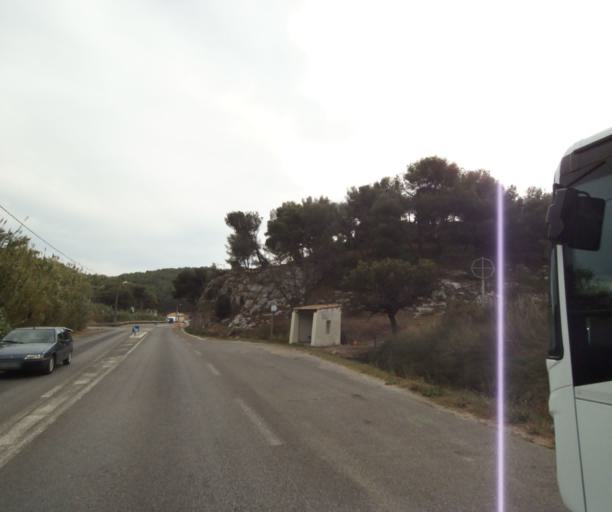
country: FR
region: Provence-Alpes-Cote d'Azur
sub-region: Departement des Bouches-du-Rhone
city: Le Rove
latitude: 43.3682
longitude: 5.2610
